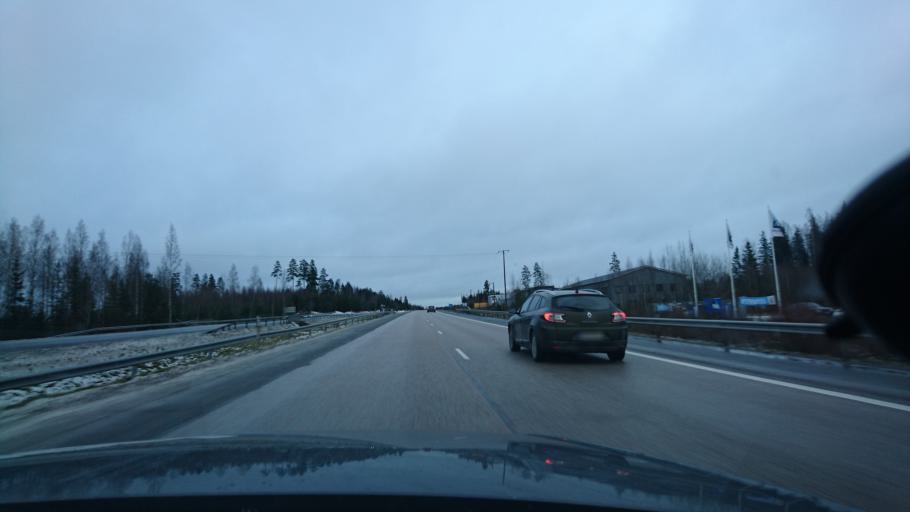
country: FI
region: Uusimaa
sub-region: Helsinki
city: Maentsaelae
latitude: 60.6185
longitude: 25.2750
